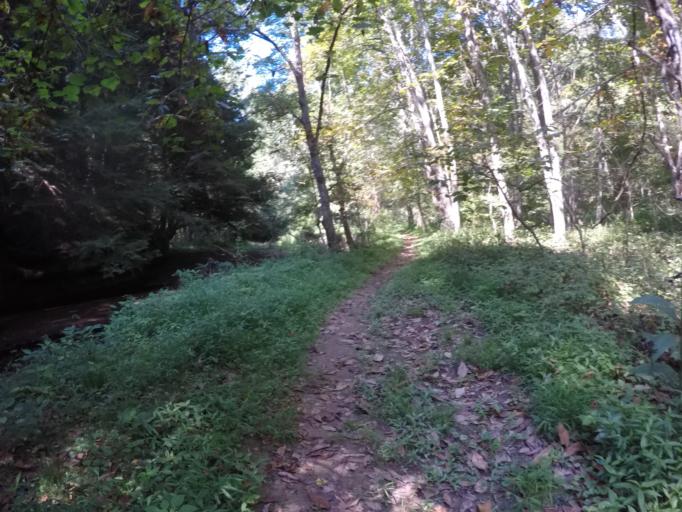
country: US
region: Ohio
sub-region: Lawrence County
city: Ironton
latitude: 38.6281
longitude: -82.6102
